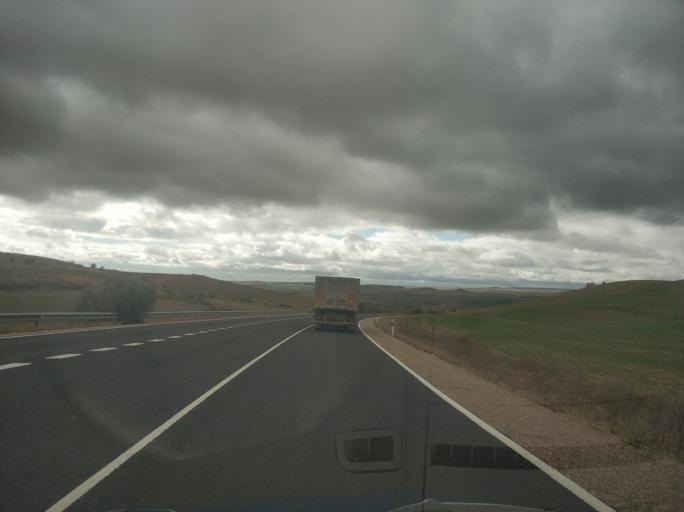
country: ES
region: Castille and Leon
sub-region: Provincia de Zamora
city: Castrillo de la Guarena
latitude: 41.2396
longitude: -5.2972
